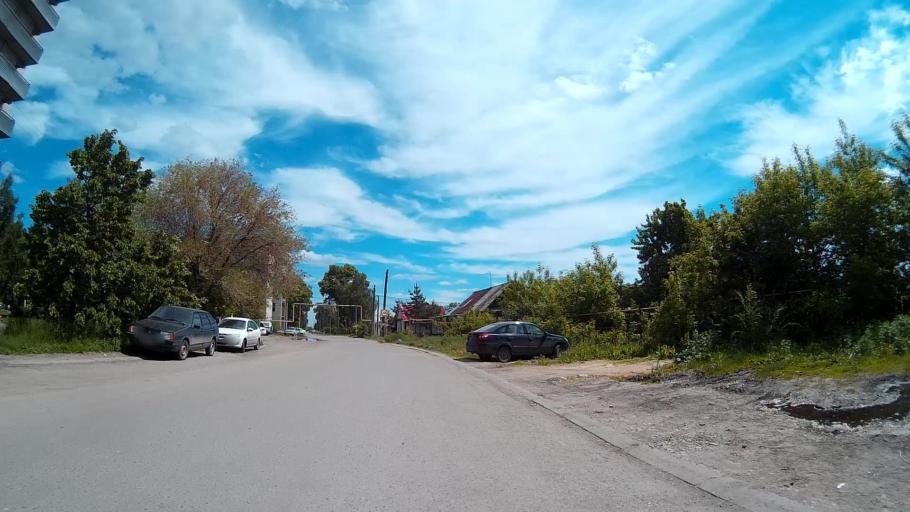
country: RU
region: Ulyanovsk
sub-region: Ulyanovskiy Rayon
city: Ulyanovsk
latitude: 54.2771
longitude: 48.3443
